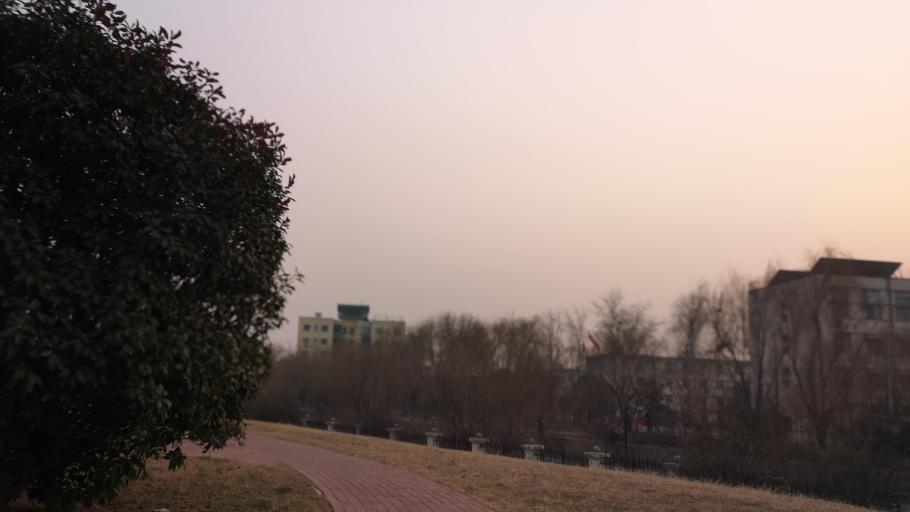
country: CN
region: Henan Sheng
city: Zhongyuanlu
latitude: 35.7894
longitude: 115.0747
